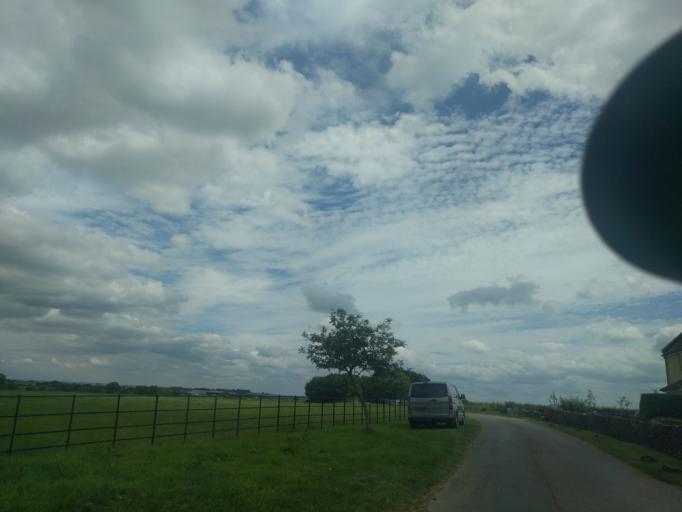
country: GB
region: England
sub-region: South Gloucestershire
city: Cold Ashton
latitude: 51.4636
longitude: -2.3634
